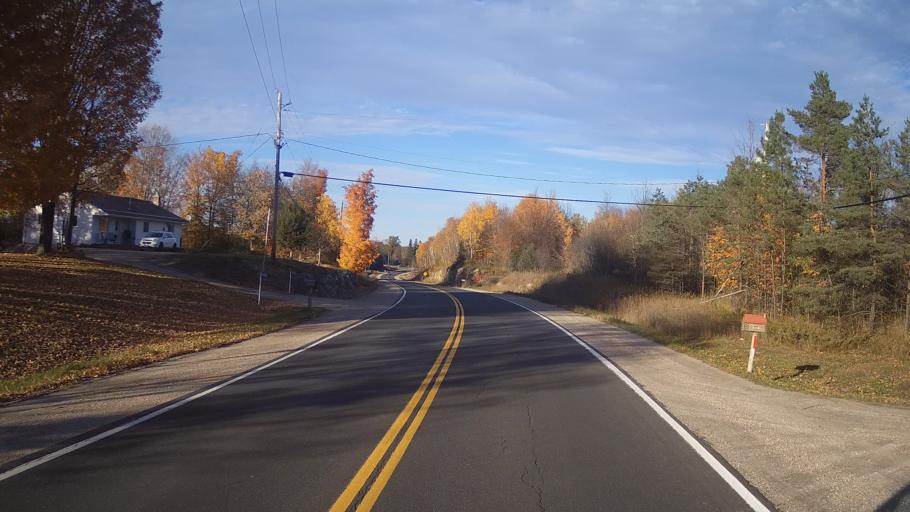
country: CA
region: Ontario
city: Perth
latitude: 44.8046
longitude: -76.3316
